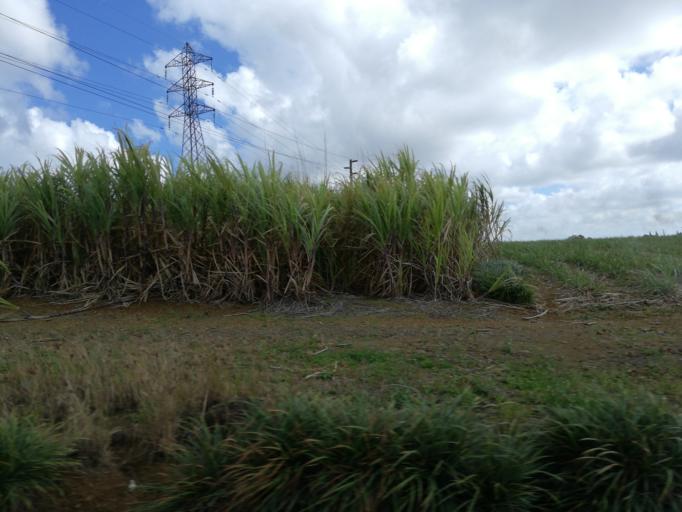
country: MU
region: Flacq
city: Queen Victoria
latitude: -20.2205
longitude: 57.6903
